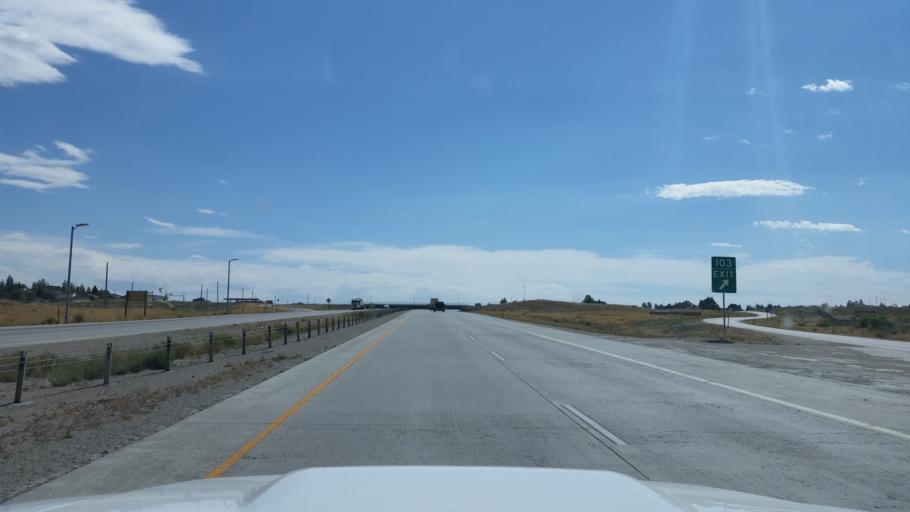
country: US
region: Wyoming
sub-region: Sweetwater County
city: Rock Springs
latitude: 41.6023
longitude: -109.2390
